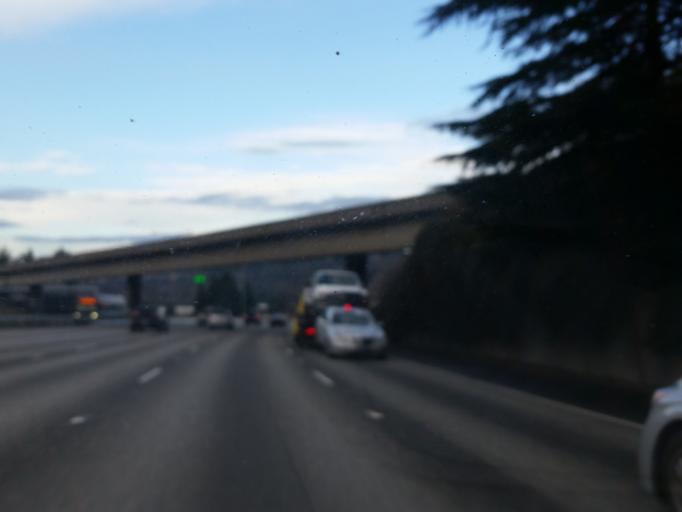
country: US
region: Washington
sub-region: King County
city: Tukwila
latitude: 47.4817
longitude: -122.2714
